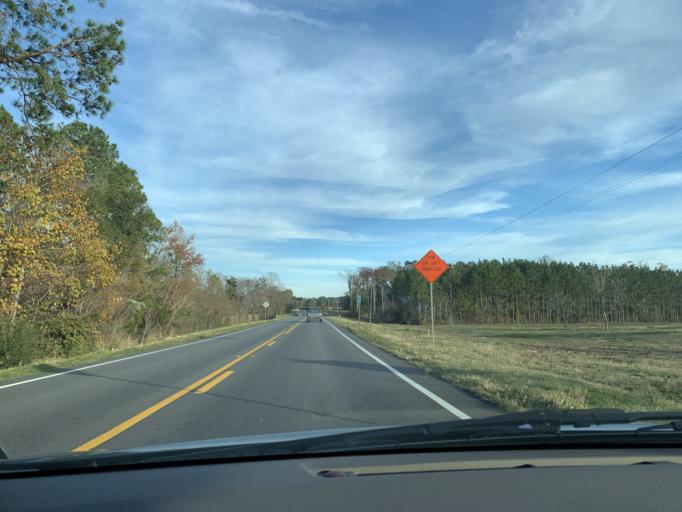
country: US
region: Georgia
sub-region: Irwin County
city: Ocilla
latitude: 31.5924
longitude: -83.2065
